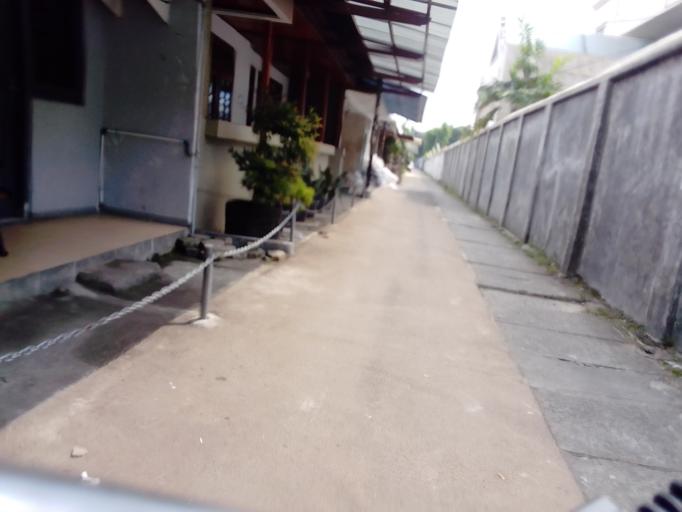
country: ID
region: Jakarta Raya
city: Jakarta
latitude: -6.2113
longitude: 106.8118
